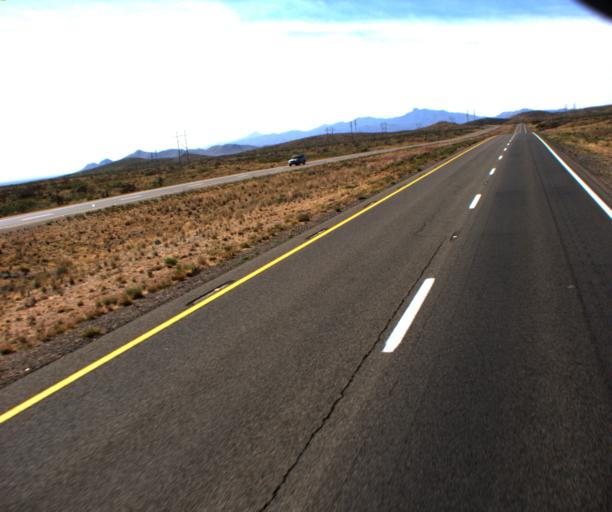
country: US
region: Arizona
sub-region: Graham County
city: Swift Trail Junction
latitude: 32.4856
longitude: -109.6735
